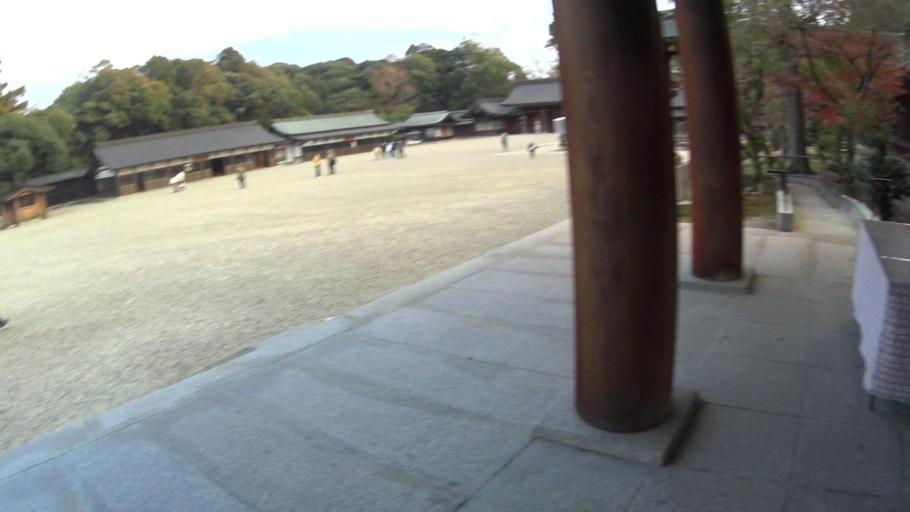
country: JP
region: Nara
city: Kashihara-shi
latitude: 34.4877
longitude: 135.7864
